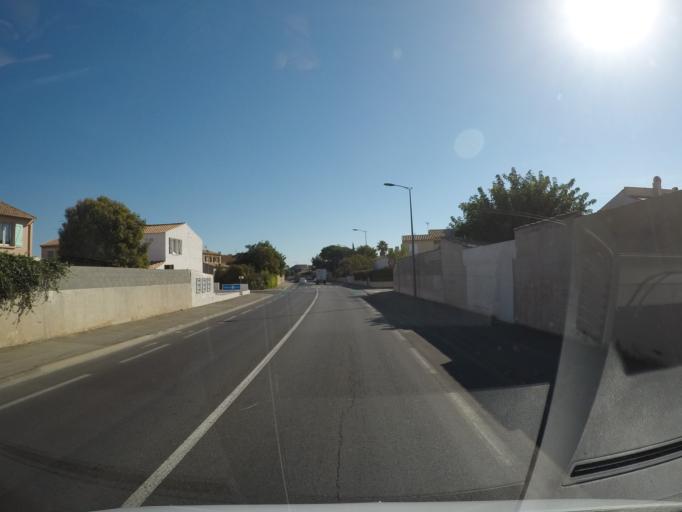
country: FR
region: Languedoc-Roussillon
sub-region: Departement de l'Aude
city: Narbonne
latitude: 43.1748
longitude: 3.0072
